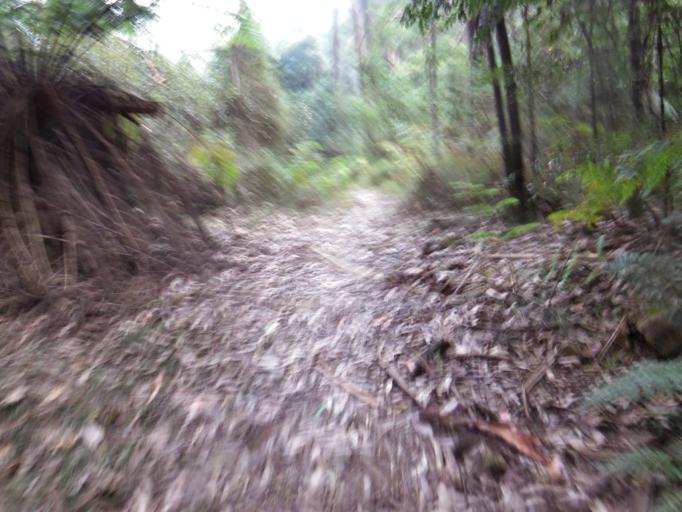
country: AU
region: Victoria
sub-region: Yarra Ranges
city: Healesville
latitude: -37.5114
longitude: 145.5191
